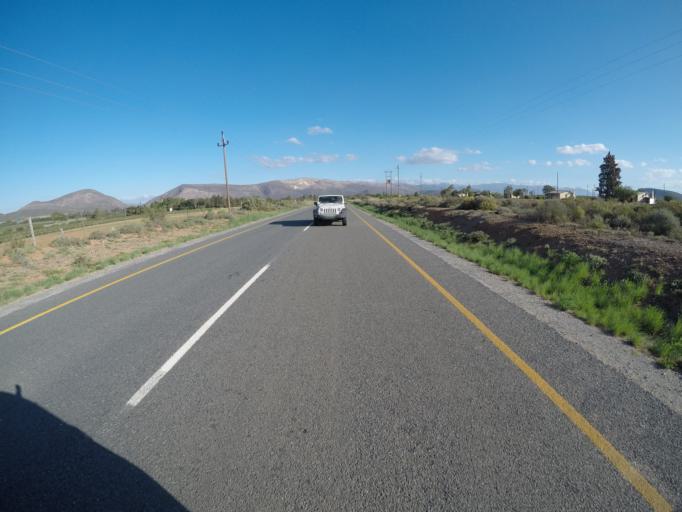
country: ZA
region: Western Cape
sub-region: Cape Winelands District Municipality
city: Ashton
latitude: -33.7993
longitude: 19.7813
